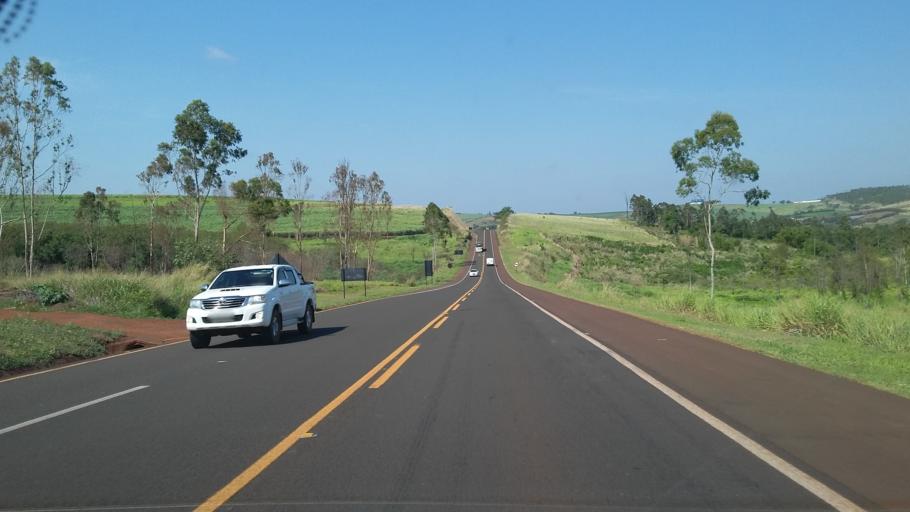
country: BR
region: Parana
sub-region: Bandeirantes
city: Bandeirantes
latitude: -23.1273
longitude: -50.3626
